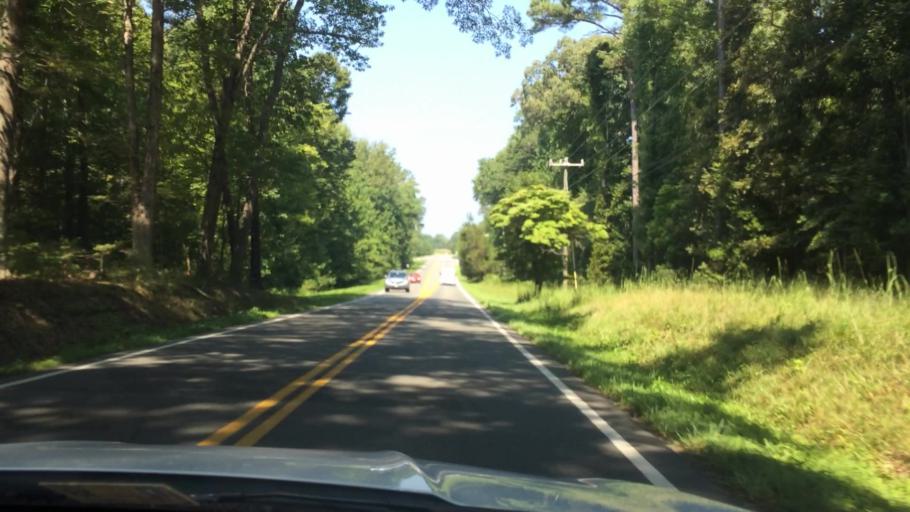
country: US
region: Virginia
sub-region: New Kent County
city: New Kent
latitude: 37.5219
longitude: -77.0047
